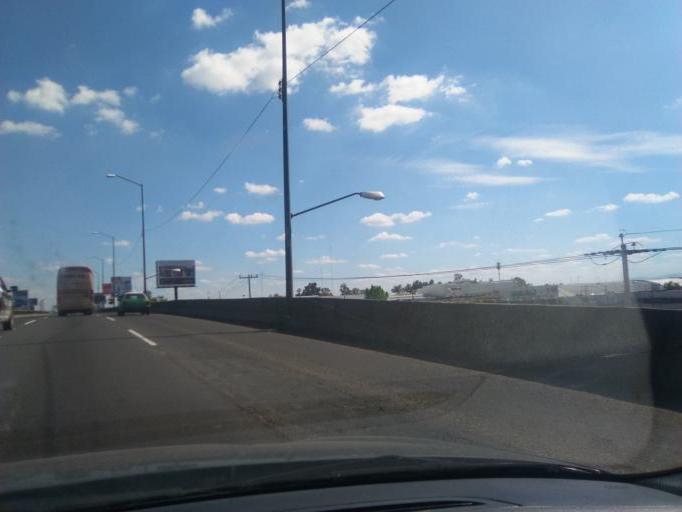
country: MX
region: Guanajuato
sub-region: Leon
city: Fraccionamiento Paraiso Real
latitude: 21.0907
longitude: -101.6213
